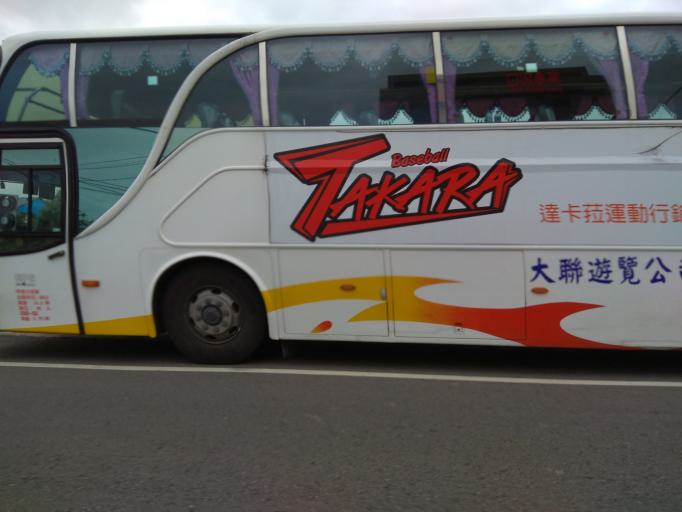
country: TW
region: Taiwan
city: Taoyuan City
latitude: 25.0485
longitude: 121.2234
